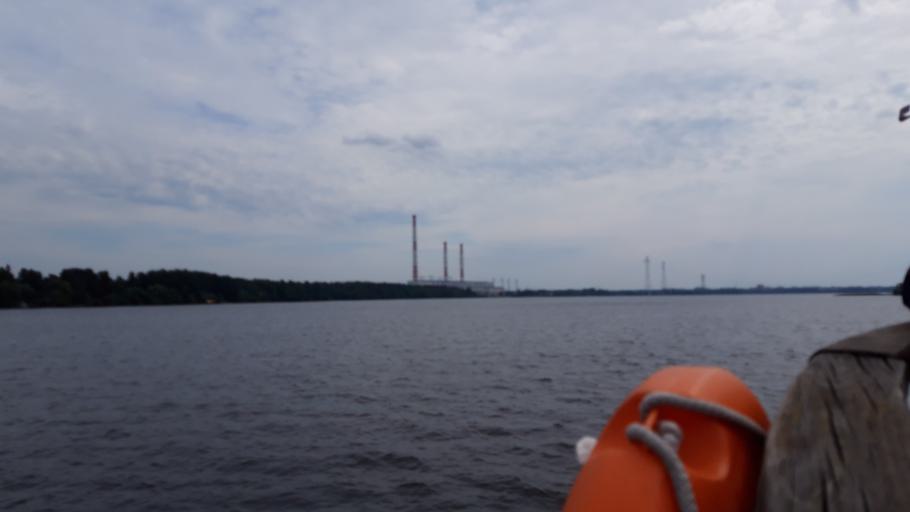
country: RU
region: Tverskaya
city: Konakovo
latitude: 56.7541
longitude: 36.7451
